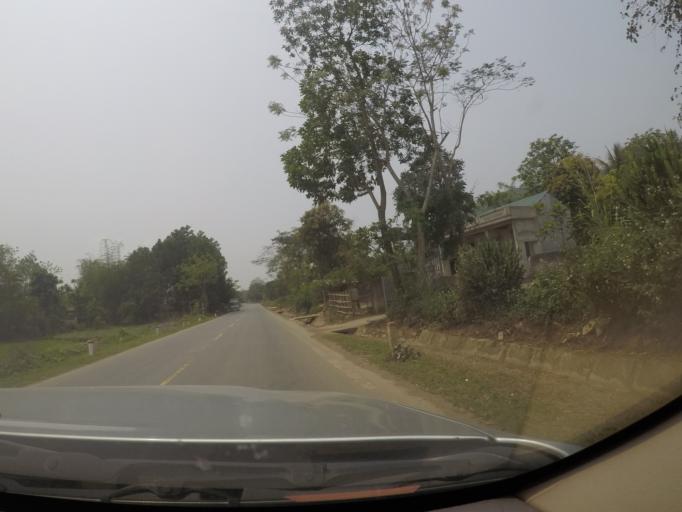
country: VN
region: Thanh Hoa
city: Thi Tran Cam Thuy
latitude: 20.1482
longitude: 105.4387
